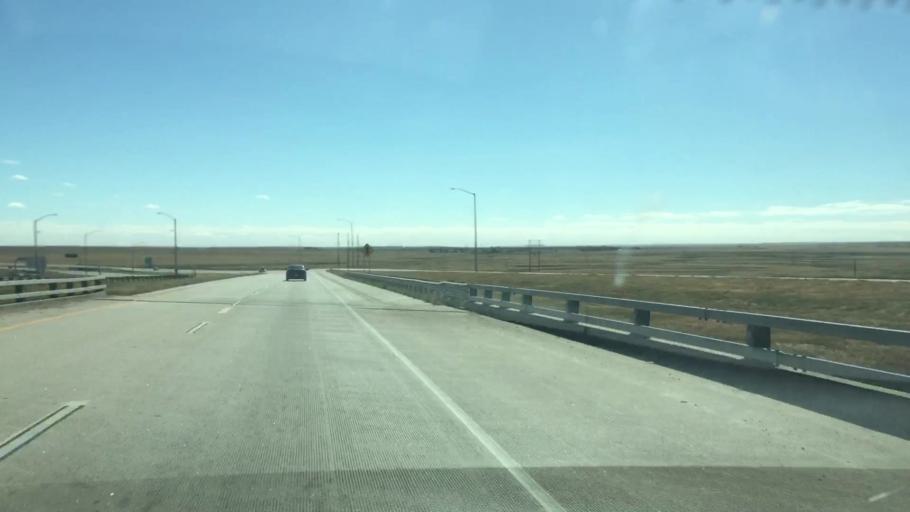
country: US
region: Colorado
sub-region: Lincoln County
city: Limon
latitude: 39.2634
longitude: -103.6662
